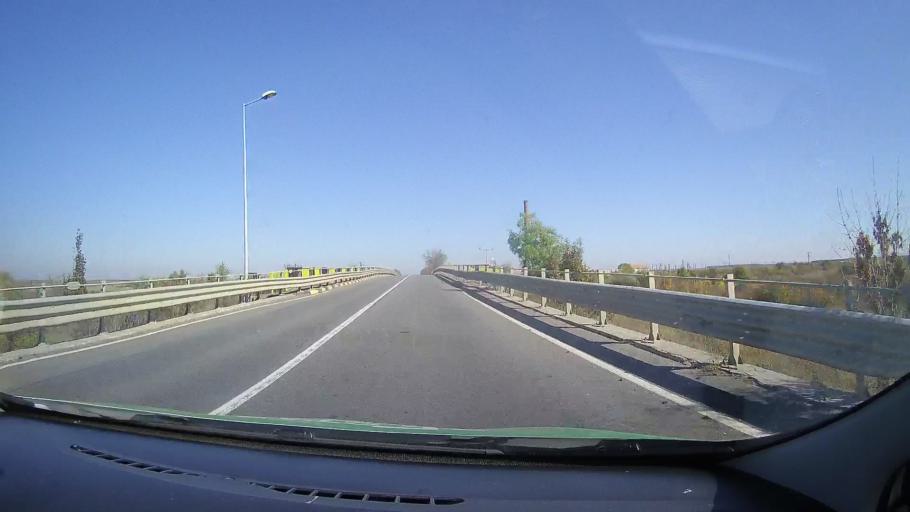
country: RO
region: Satu Mare
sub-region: Comuna Moftinu
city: Moftinu Mic
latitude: 47.7060
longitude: 22.6357
